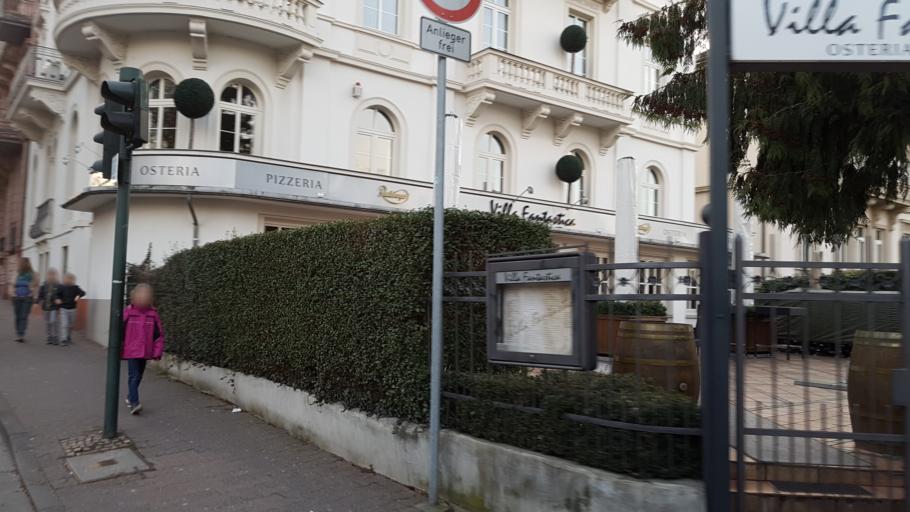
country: DE
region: Hesse
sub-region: Regierungsbezirk Darmstadt
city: Bad Homburg vor der Hoehe
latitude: 50.2284
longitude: 8.6175
